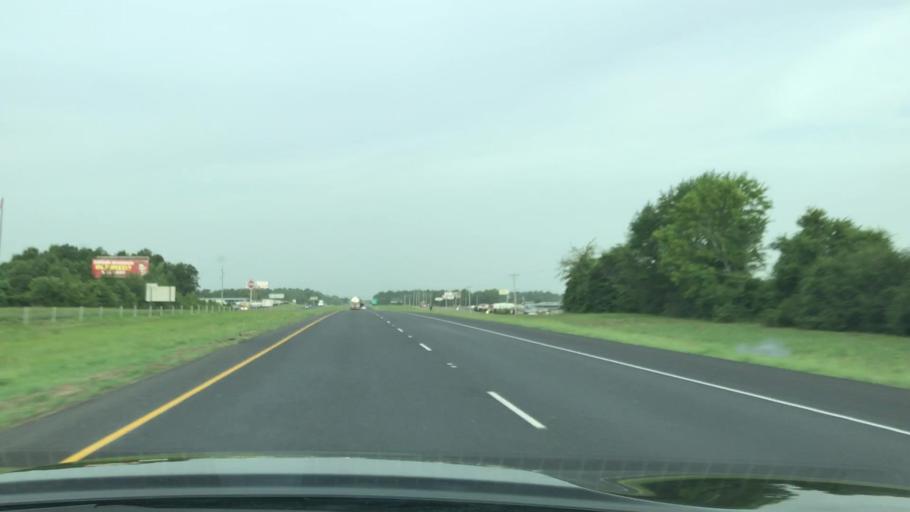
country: US
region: Louisiana
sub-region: Caddo Parish
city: Greenwood
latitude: 32.4456
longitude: -93.9191
